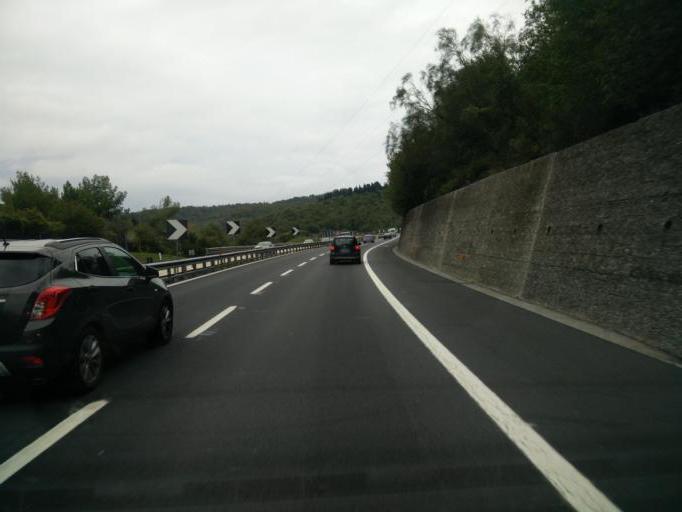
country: IT
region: Tuscany
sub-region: Province of Florence
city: Cavallina
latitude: 43.9329
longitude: 11.2197
